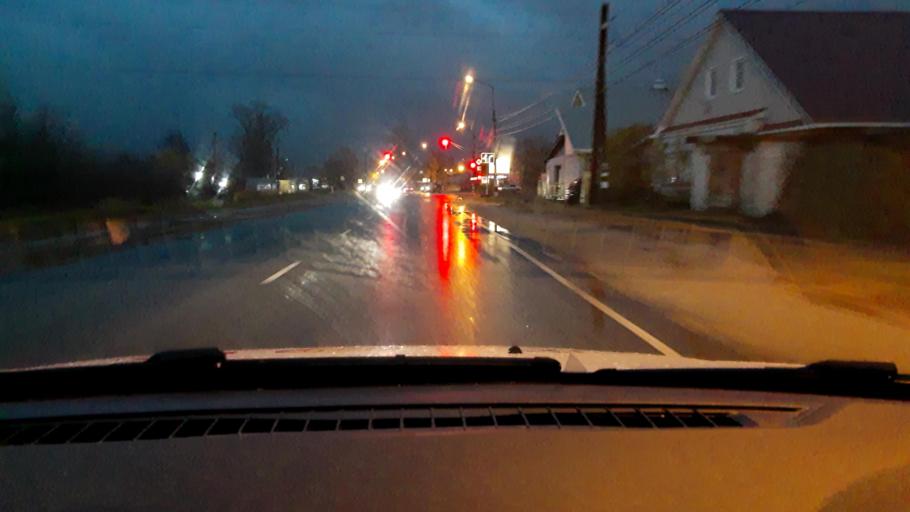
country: RU
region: Nizjnij Novgorod
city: Bor
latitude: 56.3661
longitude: 44.0839
